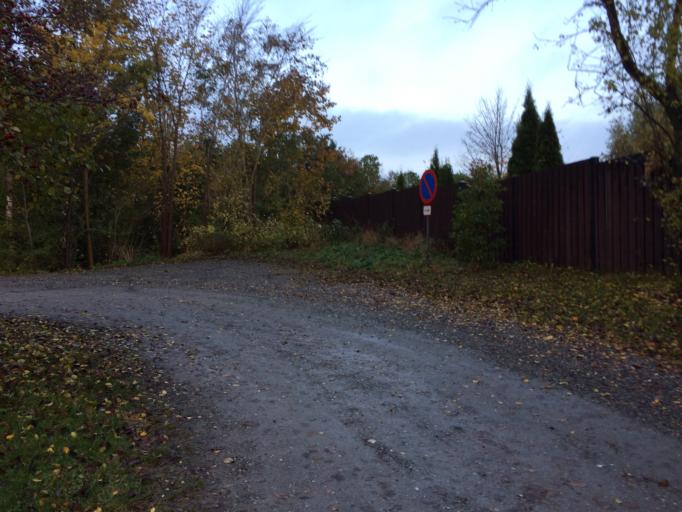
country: DK
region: Zealand
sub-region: Ringsted Kommune
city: Ringsted
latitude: 55.4827
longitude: 11.7393
